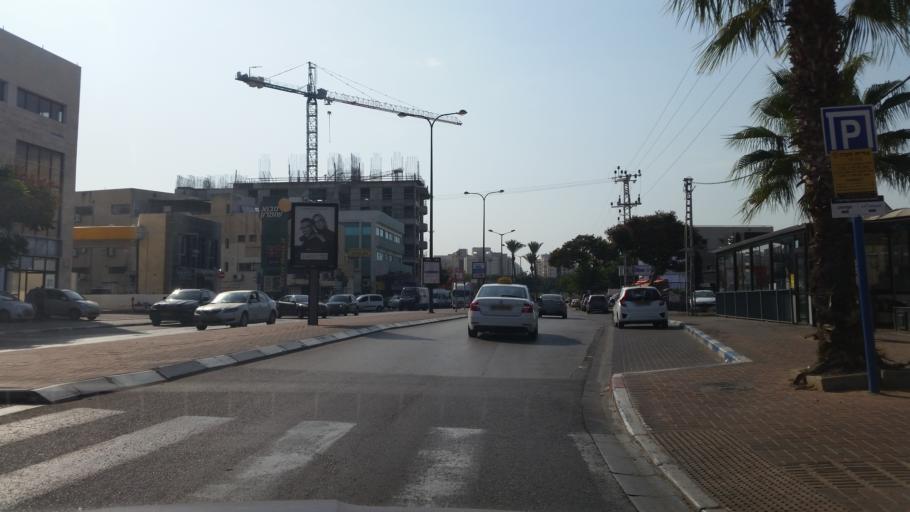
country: IL
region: Central District
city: Bet Yizhaq
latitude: 32.3153
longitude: 34.8737
